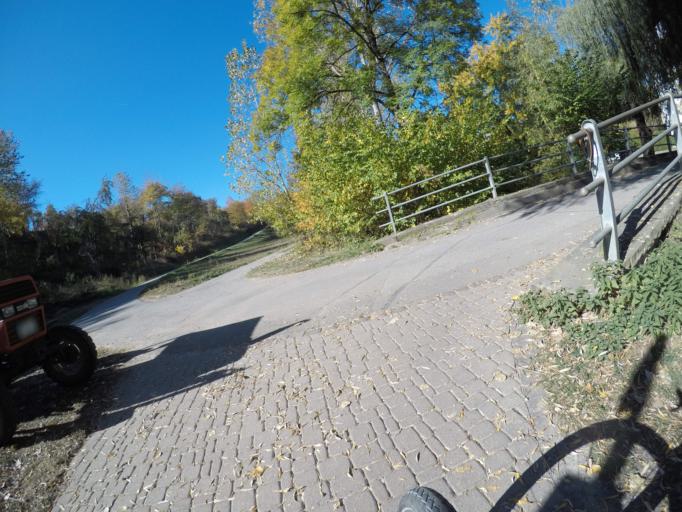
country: DE
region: Baden-Wuerttemberg
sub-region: Tuebingen Region
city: Rottenburg
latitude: 48.5354
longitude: 8.9388
